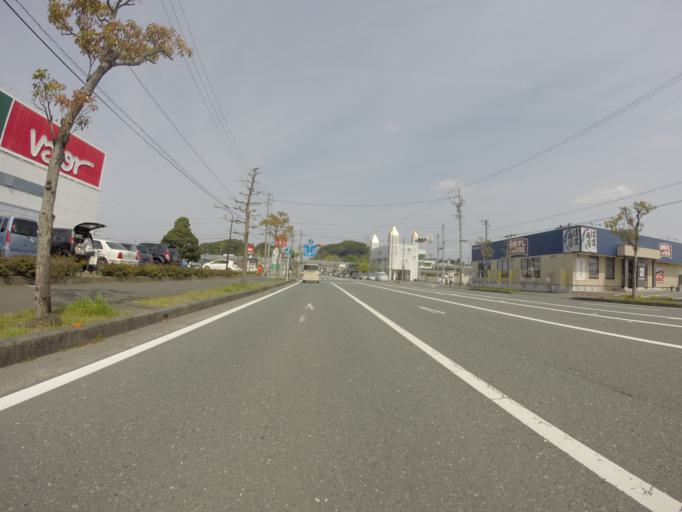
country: JP
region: Shizuoka
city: Kakegawa
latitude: 34.7767
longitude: 137.9911
